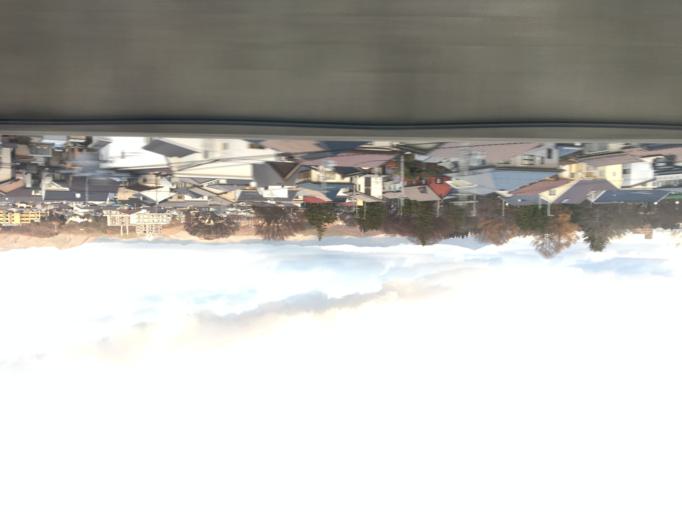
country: JP
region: Iwate
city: Morioka-shi
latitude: 39.7154
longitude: 141.1211
